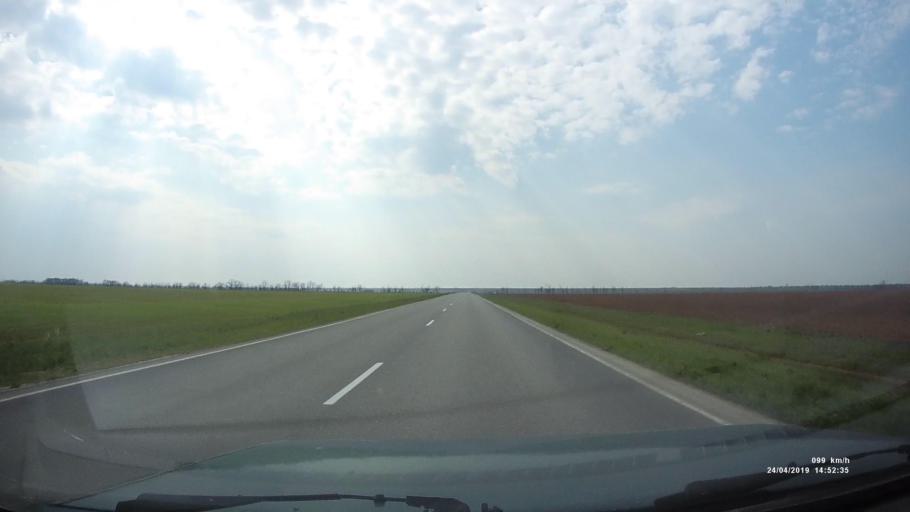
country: RU
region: Rostov
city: Remontnoye
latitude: 46.5304
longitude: 43.6776
